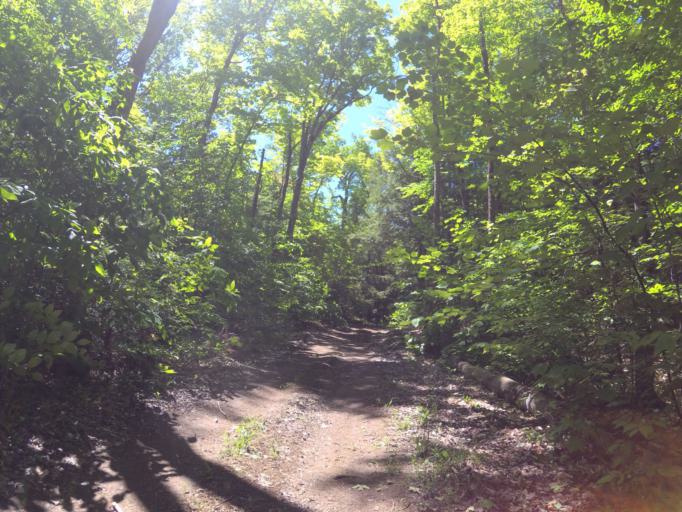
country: CA
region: Ontario
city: Renfrew
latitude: 45.0368
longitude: -77.0692
